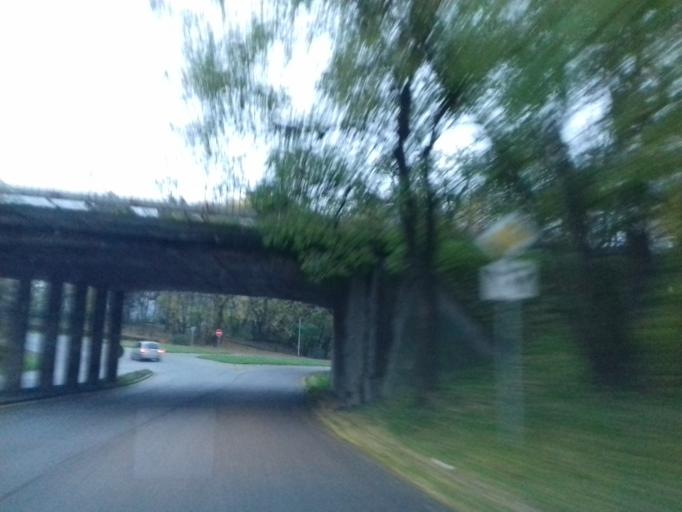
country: SK
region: Banskobystricky
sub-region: Okres Banska Bystrica
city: Banska Bystrica
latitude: 48.7409
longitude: 19.1779
